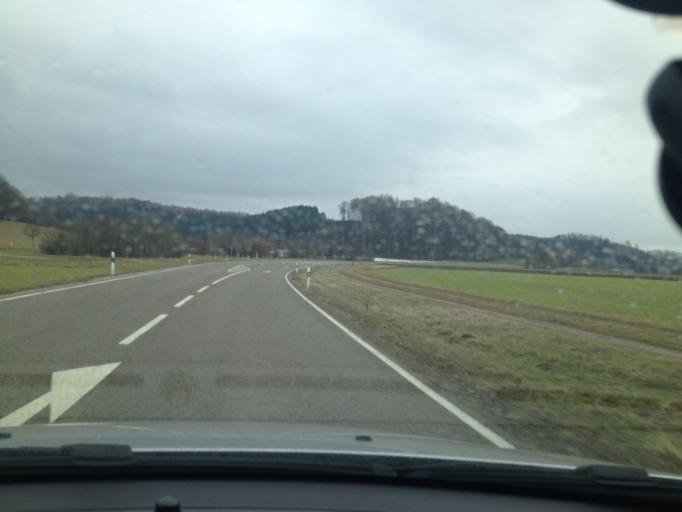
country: DE
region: Bavaria
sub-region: Swabia
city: Zusmarshausen
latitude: 48.4321
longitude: 10.5968
